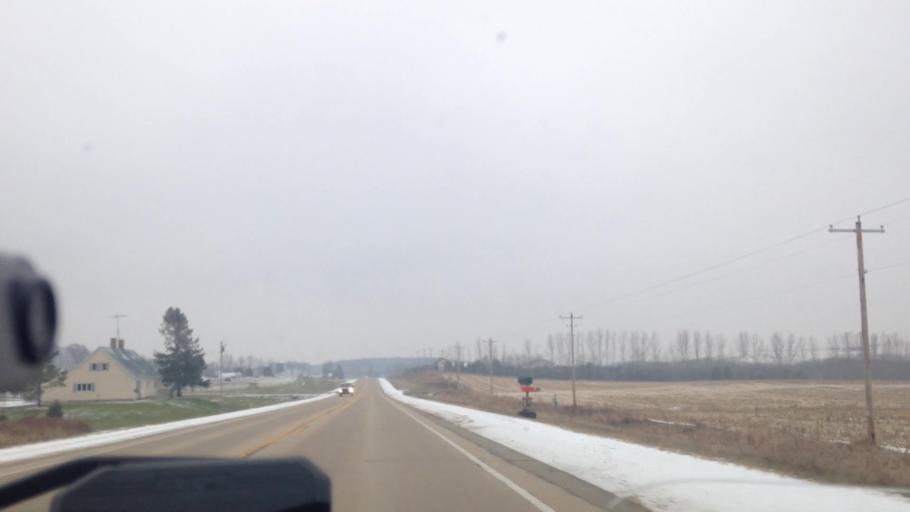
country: US
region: Wisconsin
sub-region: Dodge County
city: Mayville
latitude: 43.4741
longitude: -88.5462
